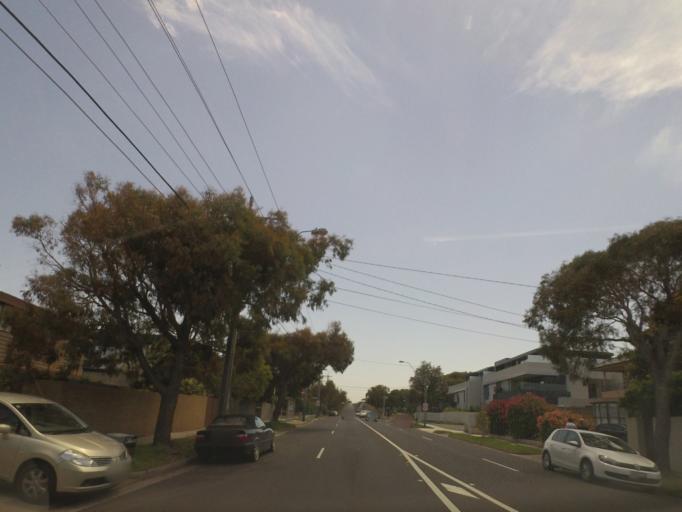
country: AU
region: Victoria
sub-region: Bayside
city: Black Rock
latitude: -37.9731
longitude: 145.0166
